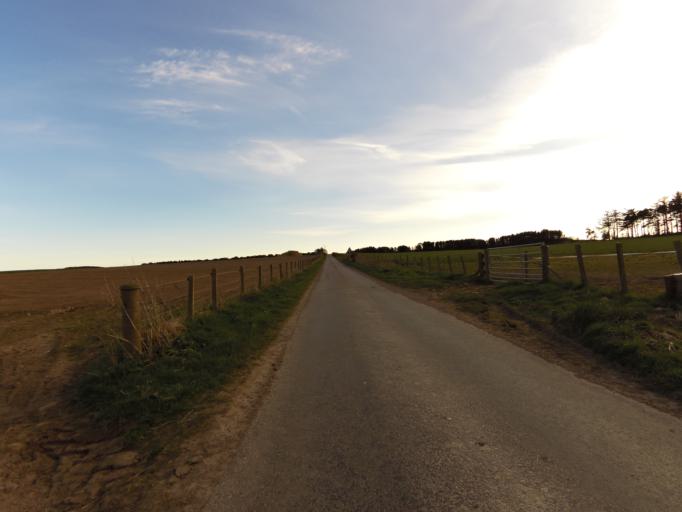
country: GB
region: Scotland
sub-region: Aberdeenshire
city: Stonehaven
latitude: 56.9416
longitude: -2.2212
